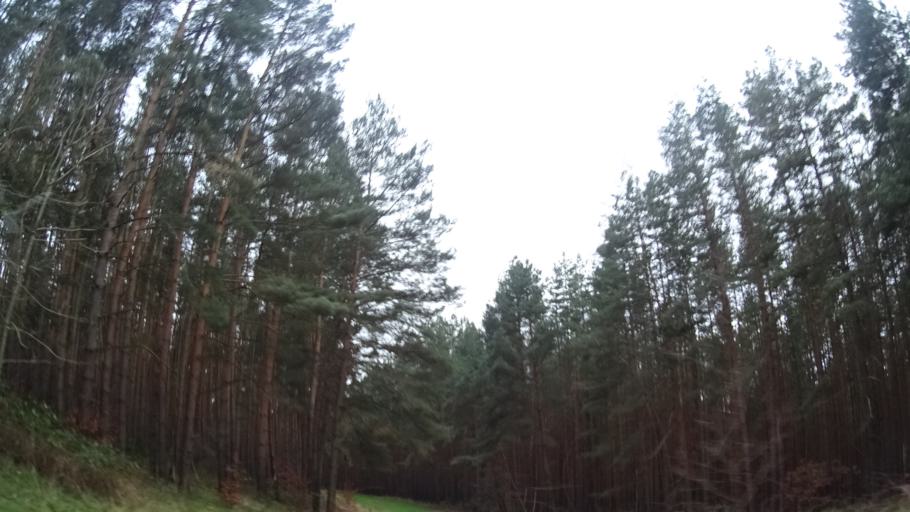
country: DE
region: Thuringia
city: Reinstadt
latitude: 50.7564
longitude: 11.4542
